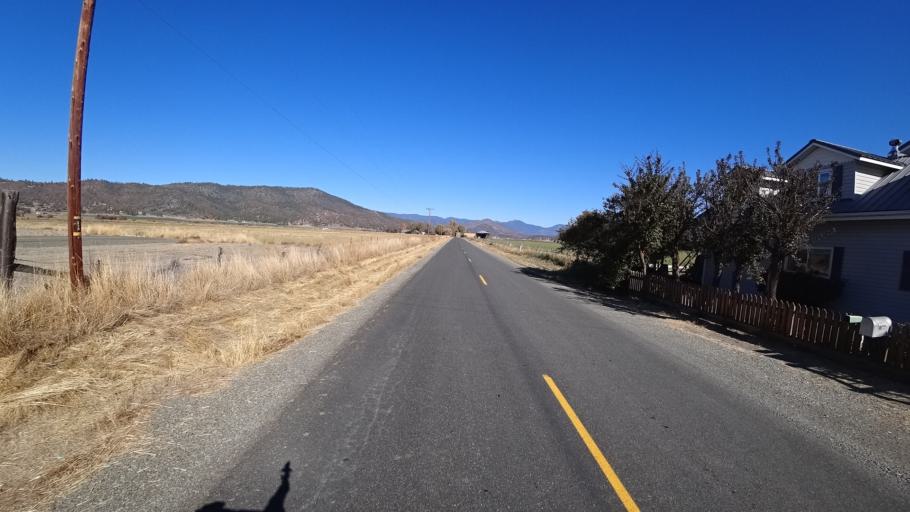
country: US
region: California
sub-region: Siskiyou County
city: Yreka
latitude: 41.5597
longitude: -122.8535
